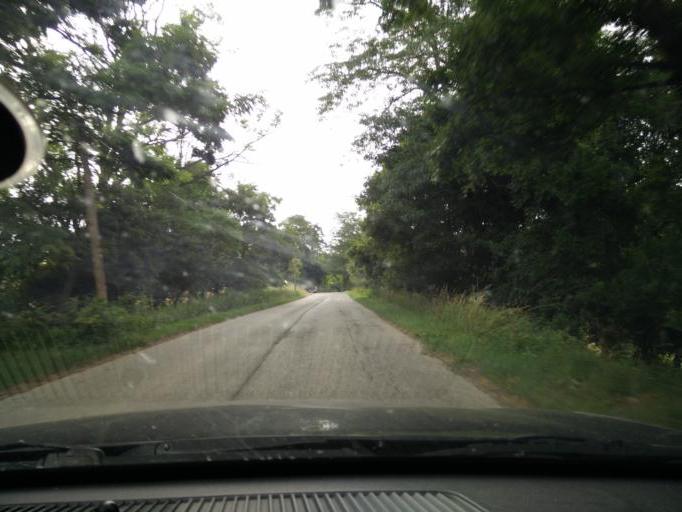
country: HU
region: Komarom-Esztergom
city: Sutto
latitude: 47.7136
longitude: 18.4506
